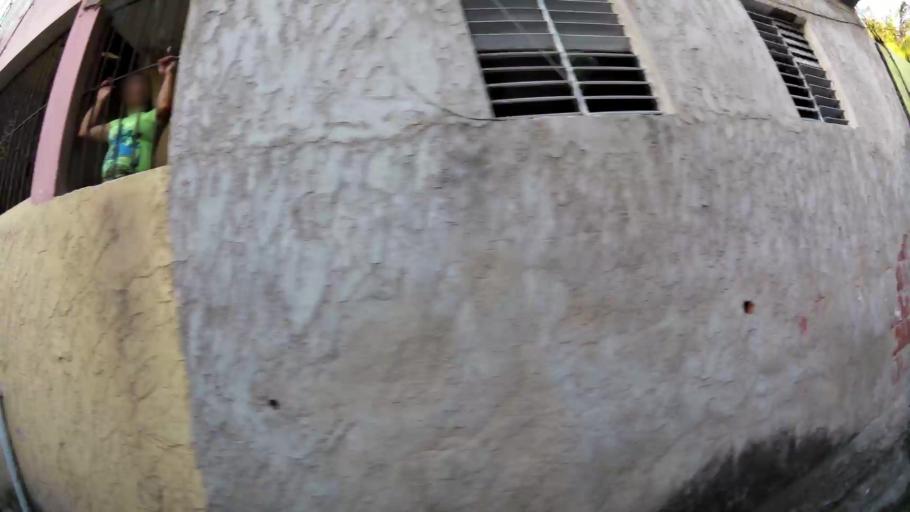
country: DO
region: Nacional
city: Santo Domingo
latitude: 18.4951
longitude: -69.9621
